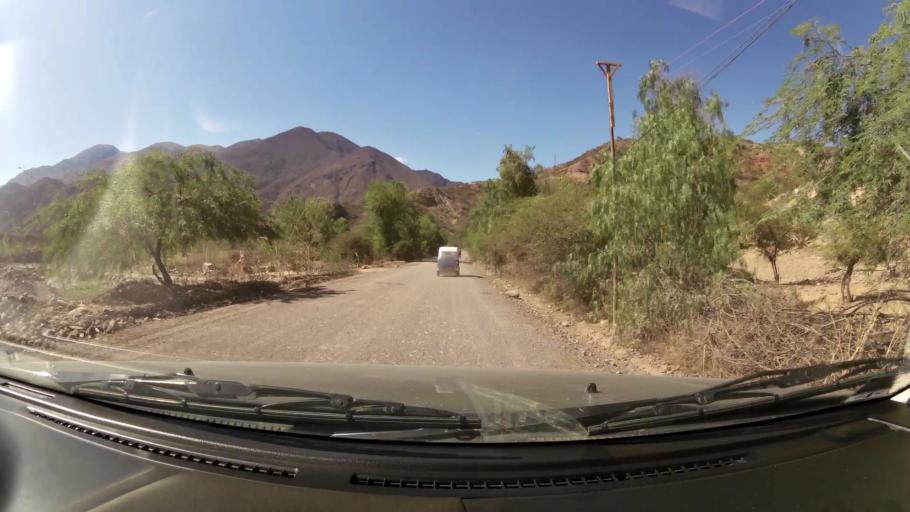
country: PE
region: Huancavelica
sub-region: Provincia de Acobamba
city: Marcas
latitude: -12.8478
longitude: -74.3315
